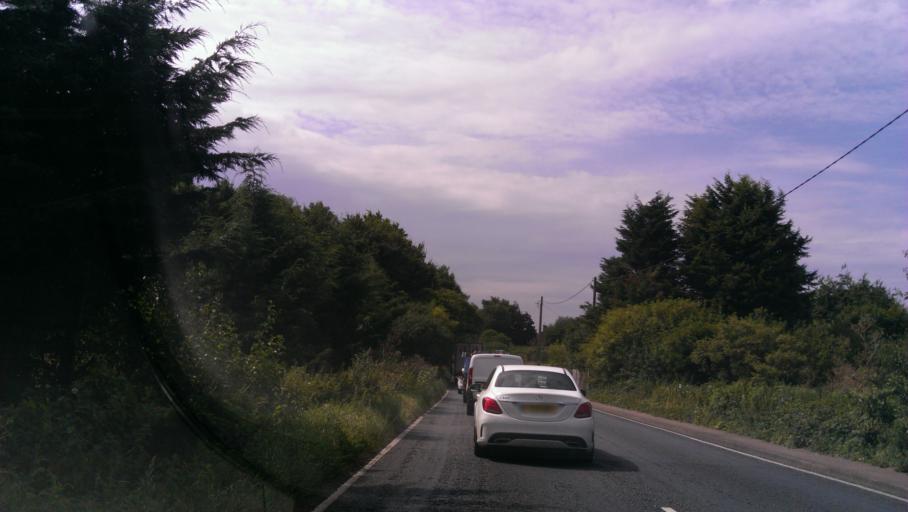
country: GB
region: England
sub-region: Kent
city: Teynham
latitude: 51.3255
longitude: 0.8091
